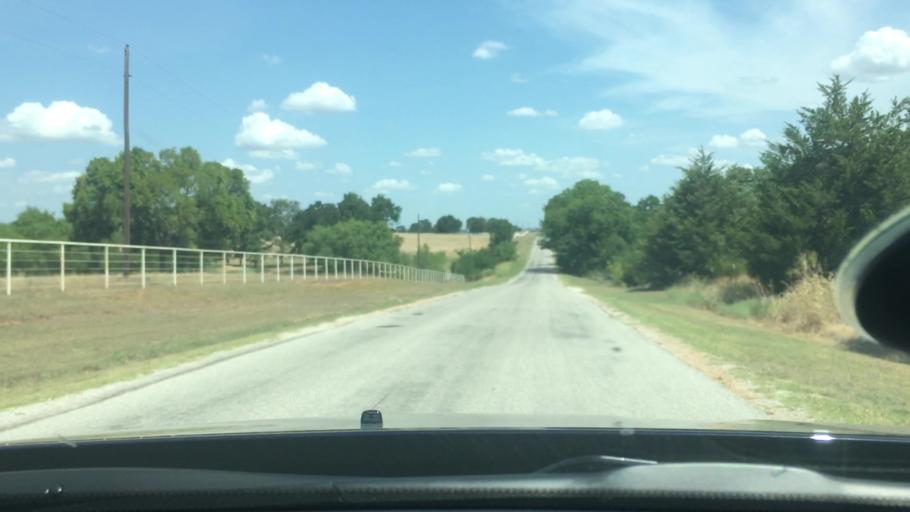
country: US
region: Oklahoma
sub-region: Love County
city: Marietta
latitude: 34.0390
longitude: -97.1957
